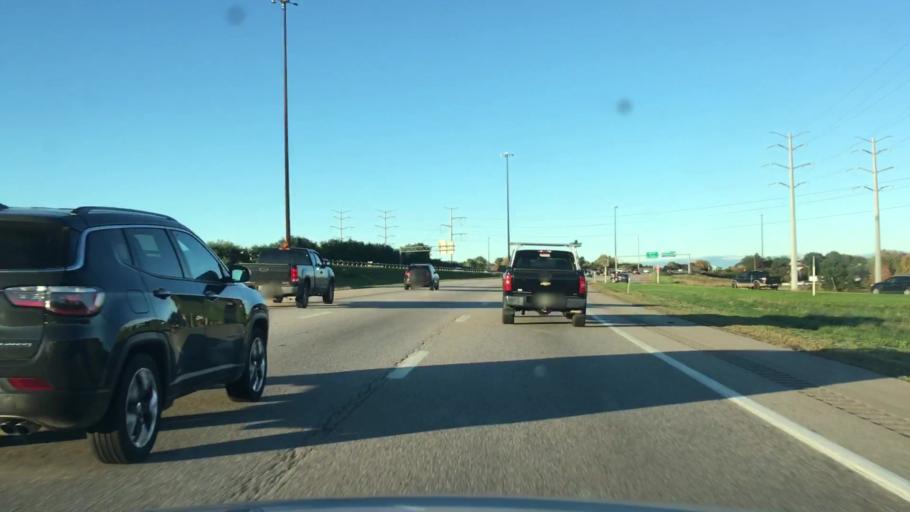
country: US
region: New Hampshire
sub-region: Rockingham County
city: Portsmouth
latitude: 43.0713
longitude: -70.7857
